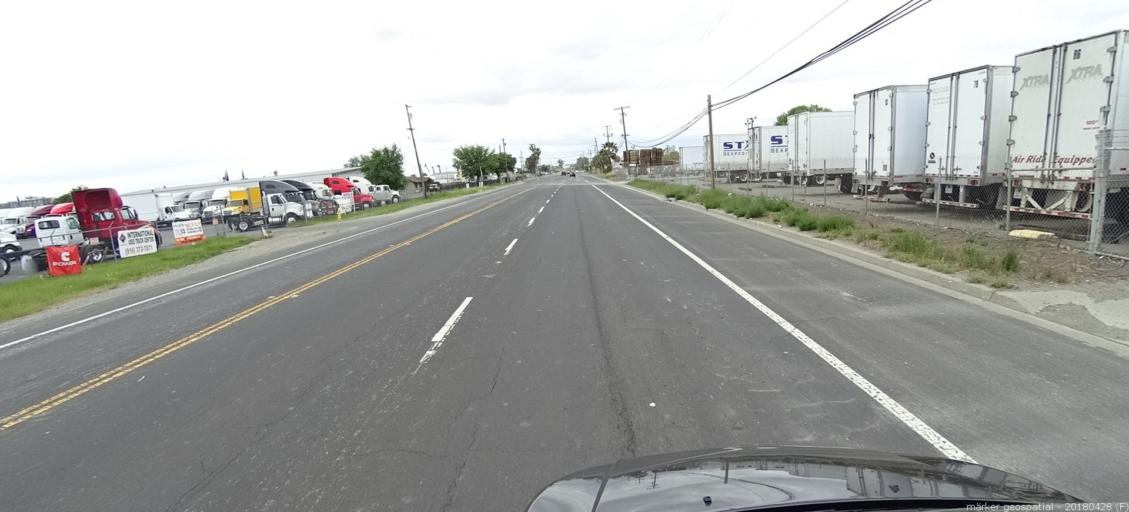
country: US
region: California
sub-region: Yolo County
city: West Sacramento
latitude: 38.5772
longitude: -121.5707
